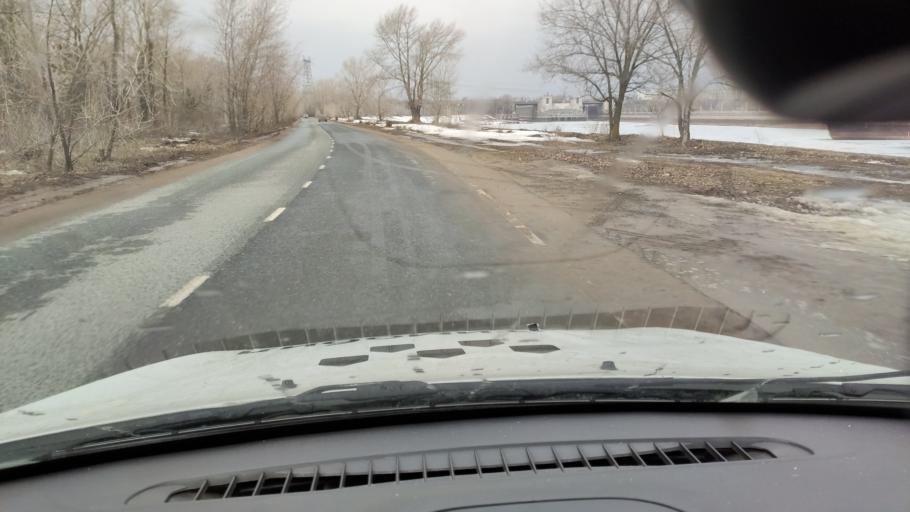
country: RU
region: Samara
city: Zhigulevsk
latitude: 53.4604
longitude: 49.5181
